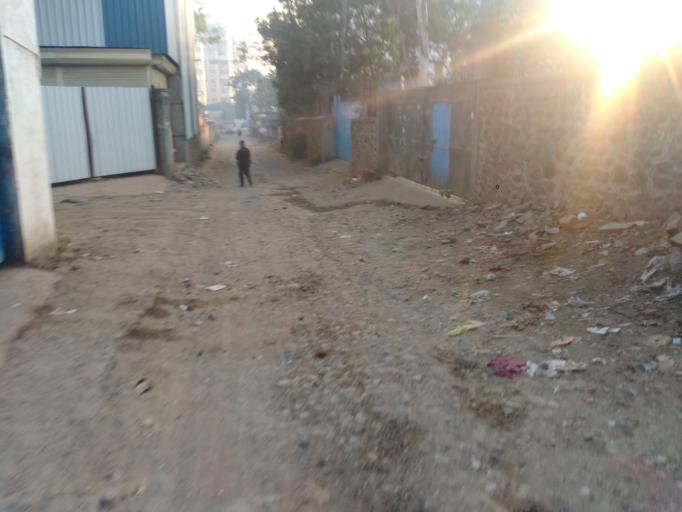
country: IN
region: Maharashtra
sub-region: Pune Division
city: Pune
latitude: 18.4455
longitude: 73.8968
